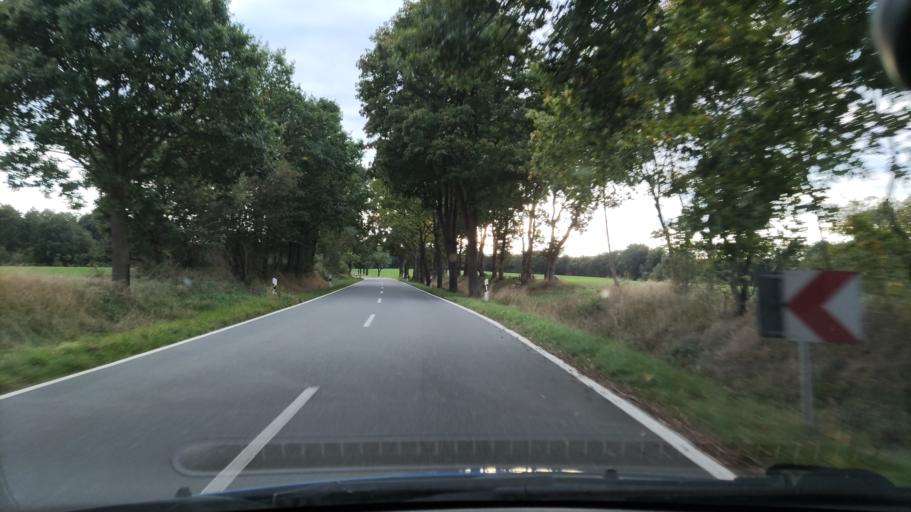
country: DE
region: Mecklenburg-Vorpommern
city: Boizenburg
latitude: 53.4132
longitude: 10.8427
